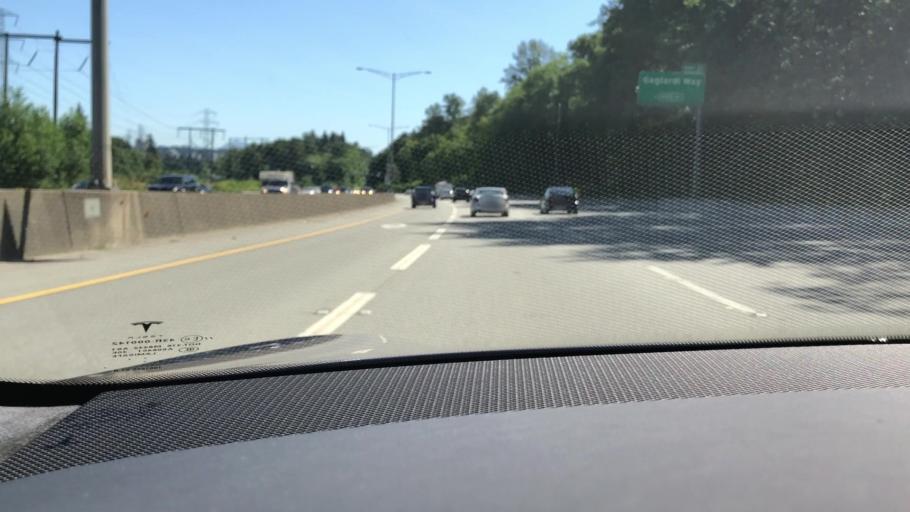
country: CA
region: British Columbia
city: New Westminster
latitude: 49.2363
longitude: -122.9295
